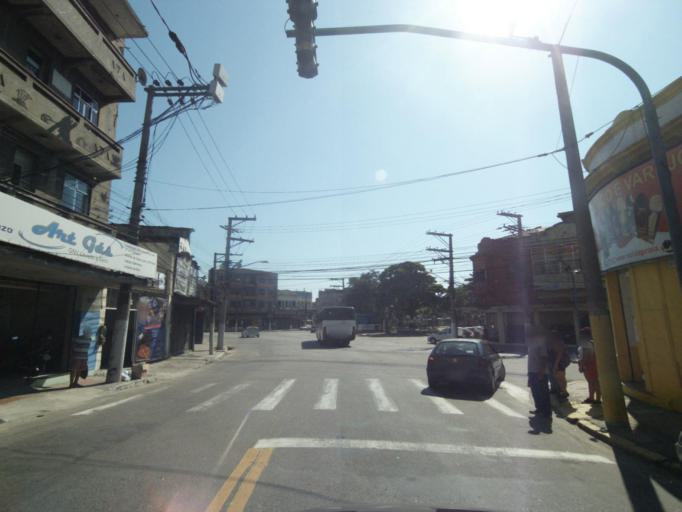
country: BR
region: Rio de Janeiro
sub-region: Niteroi
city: Niteroi
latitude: -22.8599
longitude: -43.1010
